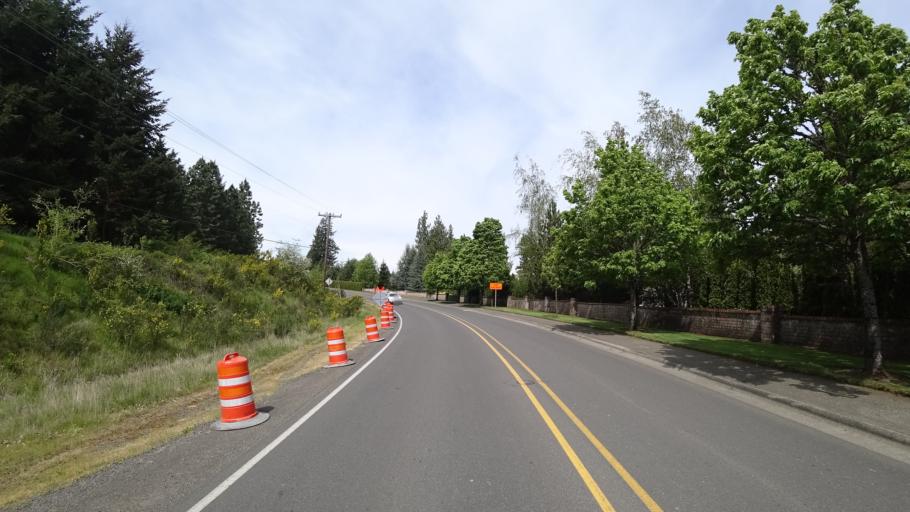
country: US
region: Oregon
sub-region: Washington County
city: Aloha
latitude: 45.4527
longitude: -122.8591
